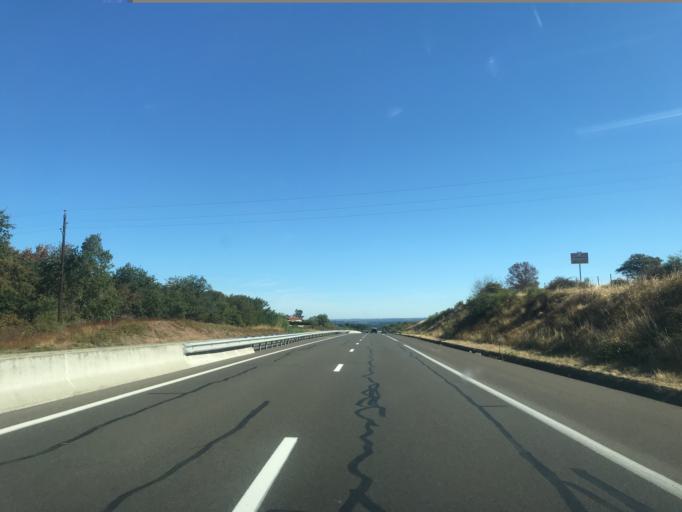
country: FR
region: Auvergne
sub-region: Departement de l'Allier
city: Quinssaines
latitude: 46.3396
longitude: 2.5365
